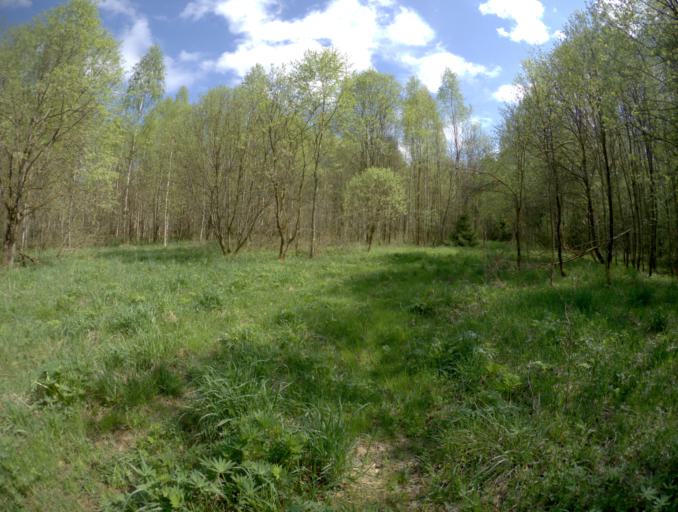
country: RU
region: Vladimir
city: Golovino
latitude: 55.9656
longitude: 40.3916
